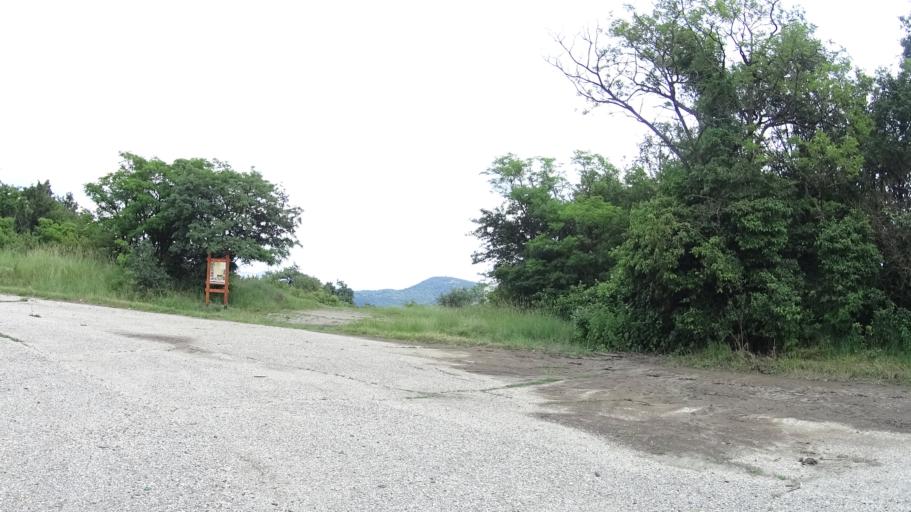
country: HU
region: Pest
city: Nagymaros
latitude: 47.7981
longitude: 18.9444
